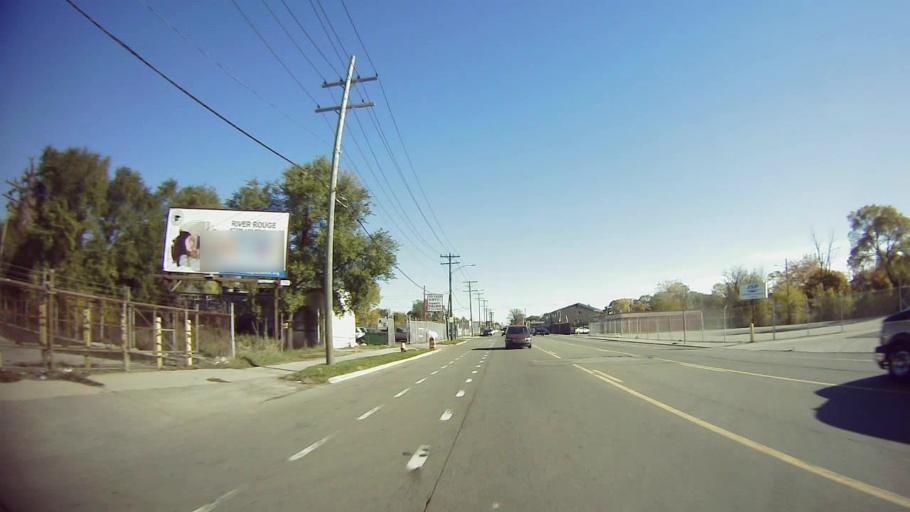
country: US
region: Michigan
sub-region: Wayne County
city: Dearborn
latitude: 42.3657
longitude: -83.1812
